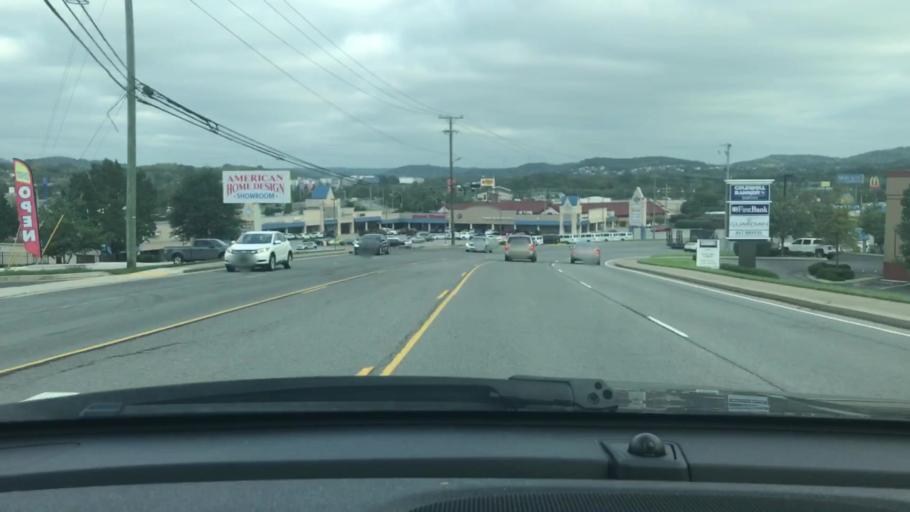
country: US
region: Tennessee
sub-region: Davidson County
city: Goodlettsville
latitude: 36.3206
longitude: -86.7013
